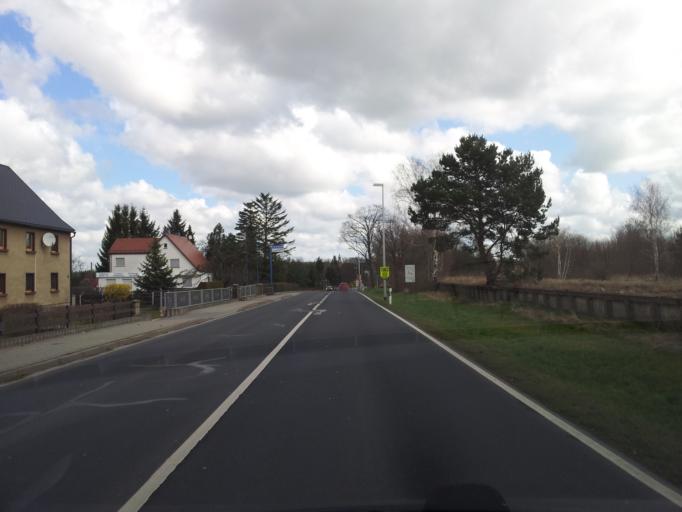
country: DE
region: Saxony
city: Laussnitz
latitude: 51.2580
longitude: 13.8924
